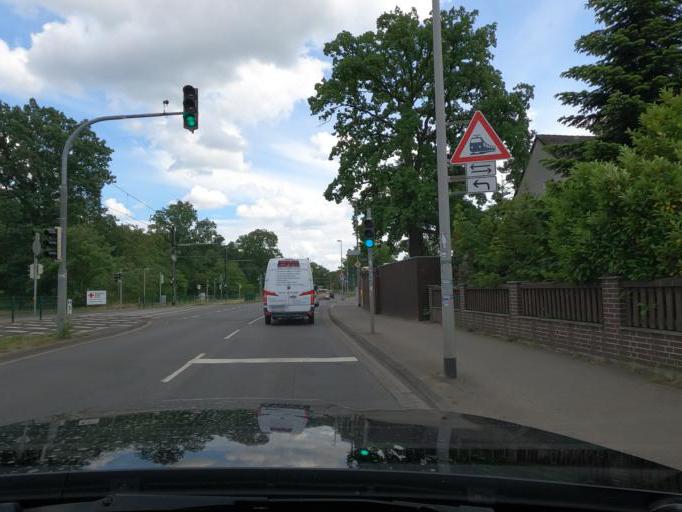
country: DE
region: Lower Saxony
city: Isernhagen Farster Bauerschaft
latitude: 52.3989
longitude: 9.8323
